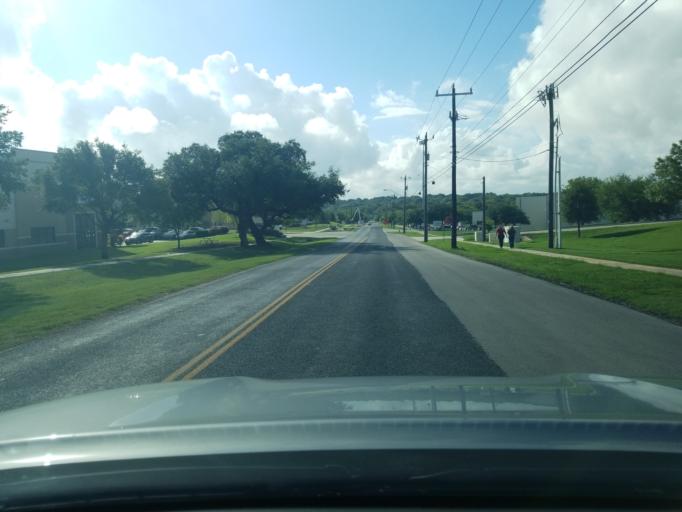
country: US
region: Texas
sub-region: Bexar County
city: Live Oak
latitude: 29.6002
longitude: -98.3643
